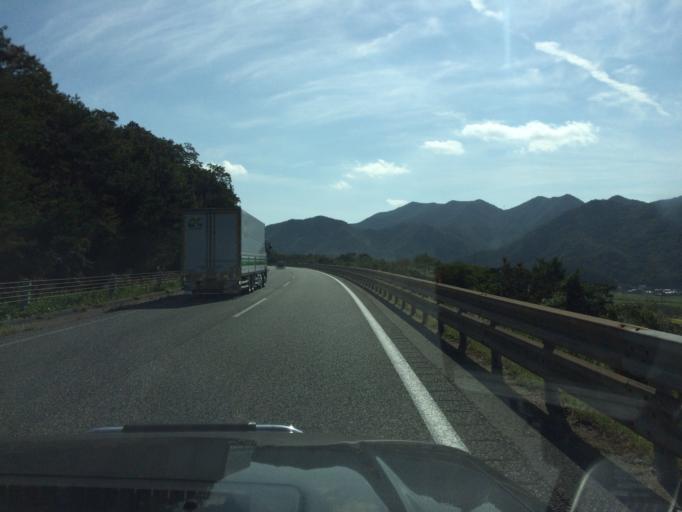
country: JP
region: Hyogo
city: Sasayama
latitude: 35.0090
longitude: 135.1605
